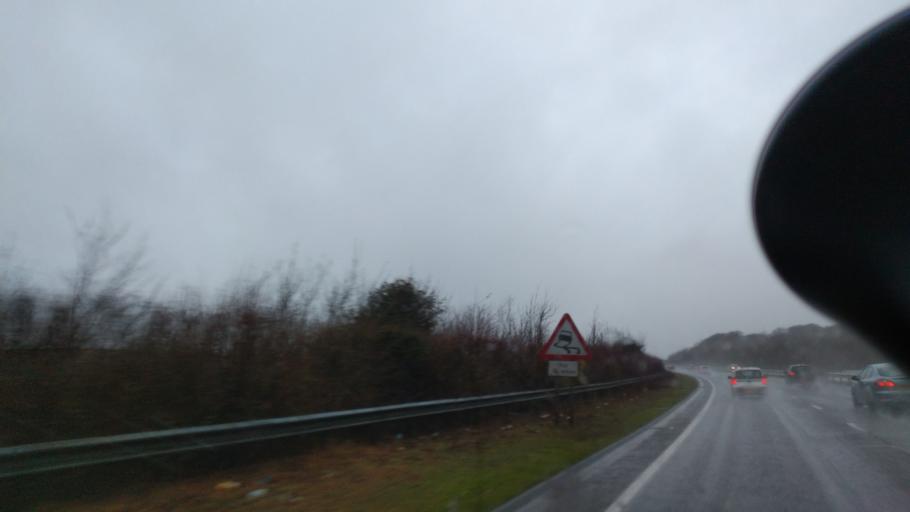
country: GB
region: England
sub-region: Brighton and Hove
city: Brighton
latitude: 50.8670
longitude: -0.1105
